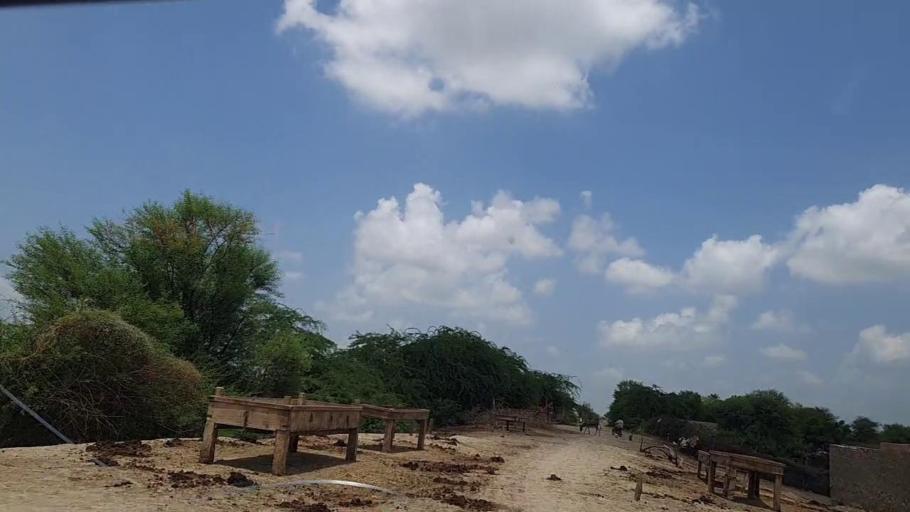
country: PK
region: Sindh
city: Tharu Shah
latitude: 26.9581
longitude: 68.0272
